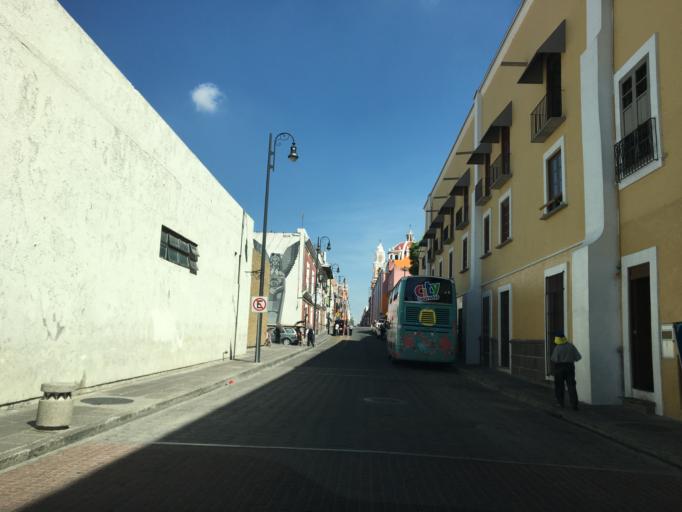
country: MX
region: Puebla
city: Puebla
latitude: 19.0402
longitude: -98.1961
